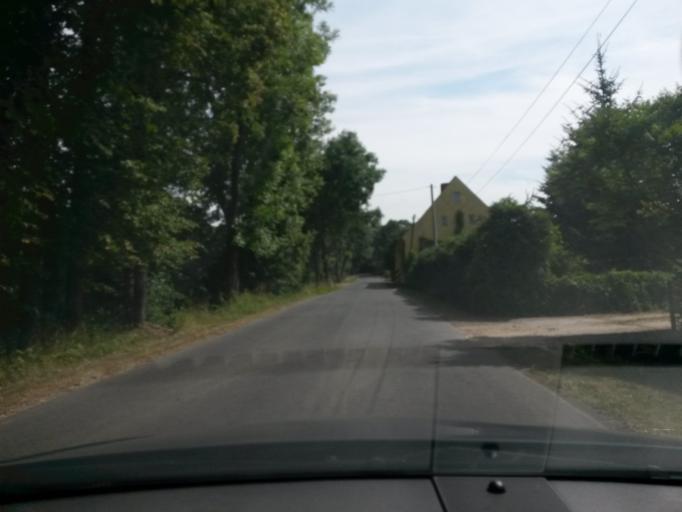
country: PL
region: Lower Silesian Voivodeship
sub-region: Powiat jaworski
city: Bolkow
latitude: 50.9772
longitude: 16.0352
